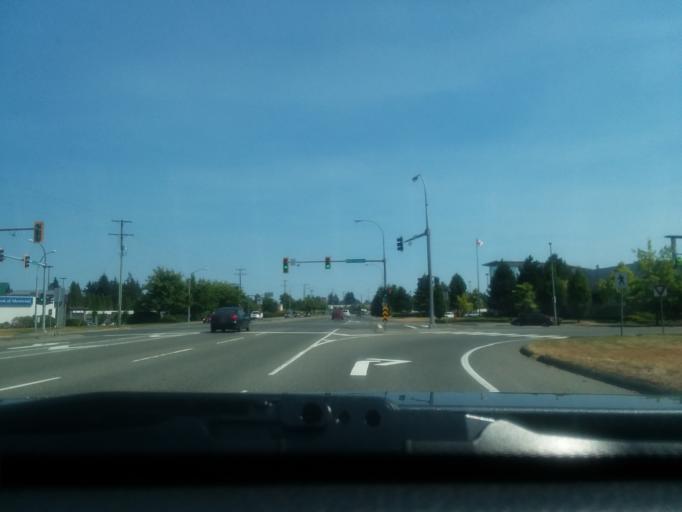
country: CA
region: British Columbia
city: Nanaimo
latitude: 49.2402
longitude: -124.0548
